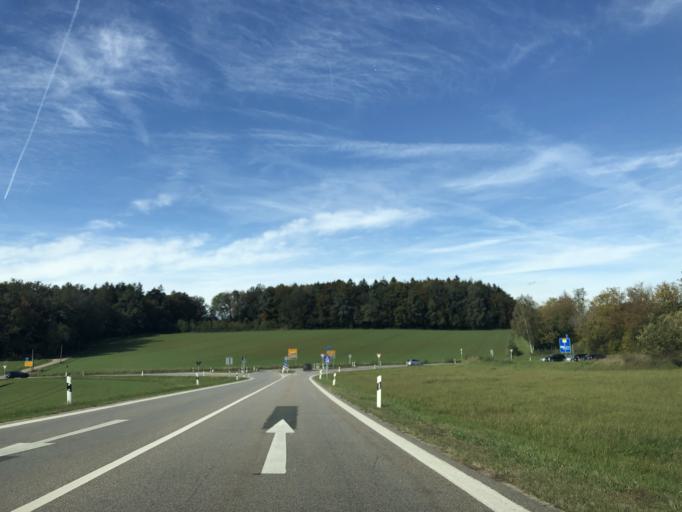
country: DE
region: Bavaria
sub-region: Upper Palatinate
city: Brunn
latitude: 49.0886
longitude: 11.8876
